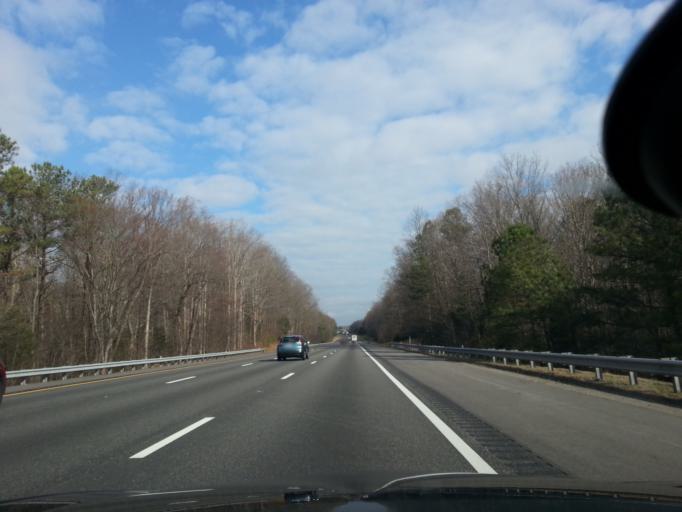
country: US
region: Virginia
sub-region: Caroline County
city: Bowling Green
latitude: 38.0557
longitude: -77.5022
